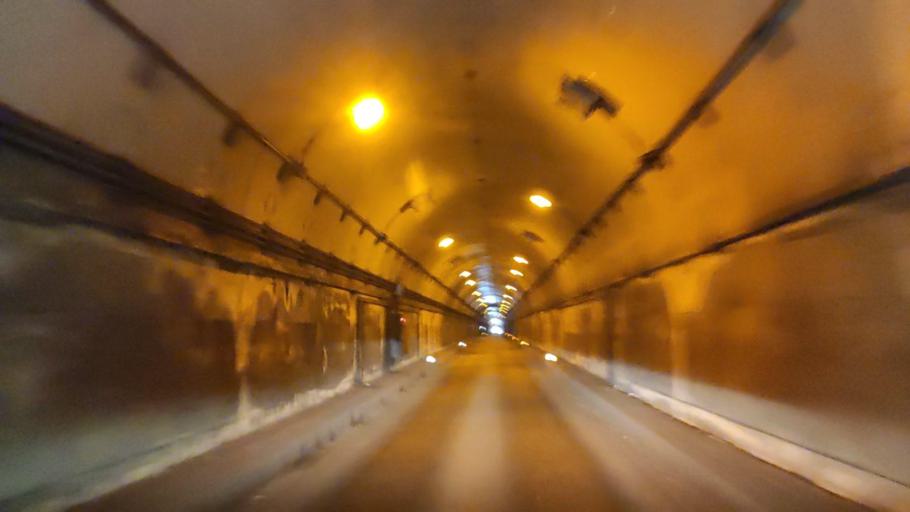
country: JP
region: Gifu
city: Gifu-shi
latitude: 35.4197
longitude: 136.7730
